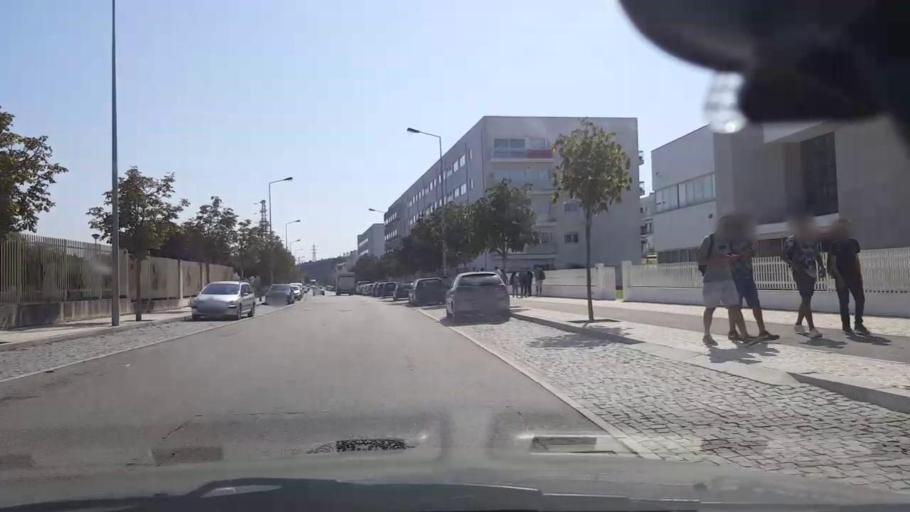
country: PT
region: Porto
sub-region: Vila do Conde
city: Vila do Conde
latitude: 41.3585
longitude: -8.7324
